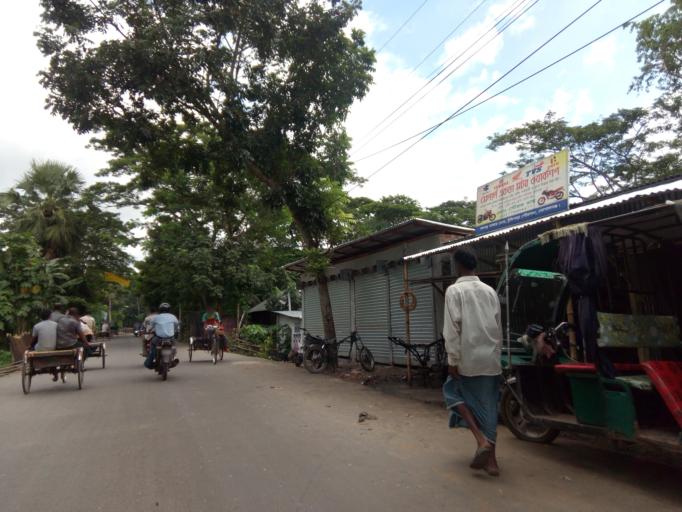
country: BD
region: Dhaka
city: Tungipara
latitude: 22.8964
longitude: 89.8906
